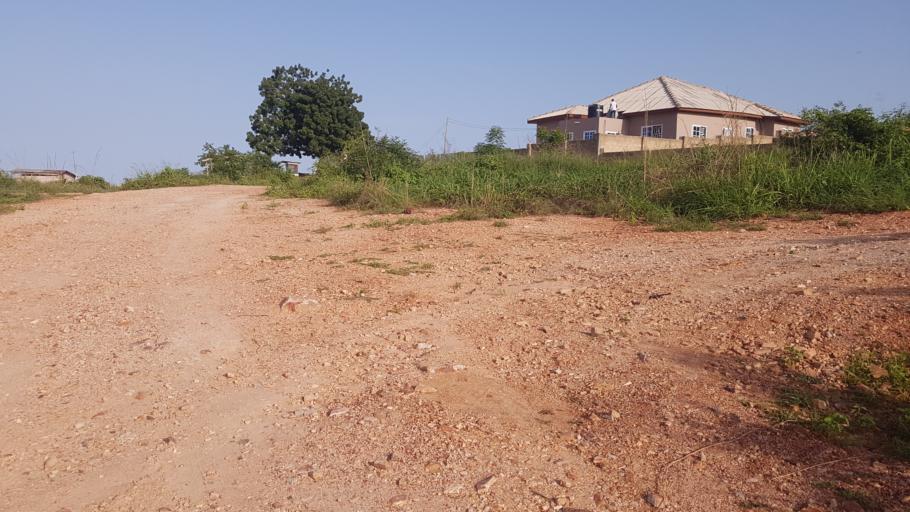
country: GH
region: Greater Accra
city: Gbawe
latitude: 5.5200
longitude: -0.3387
